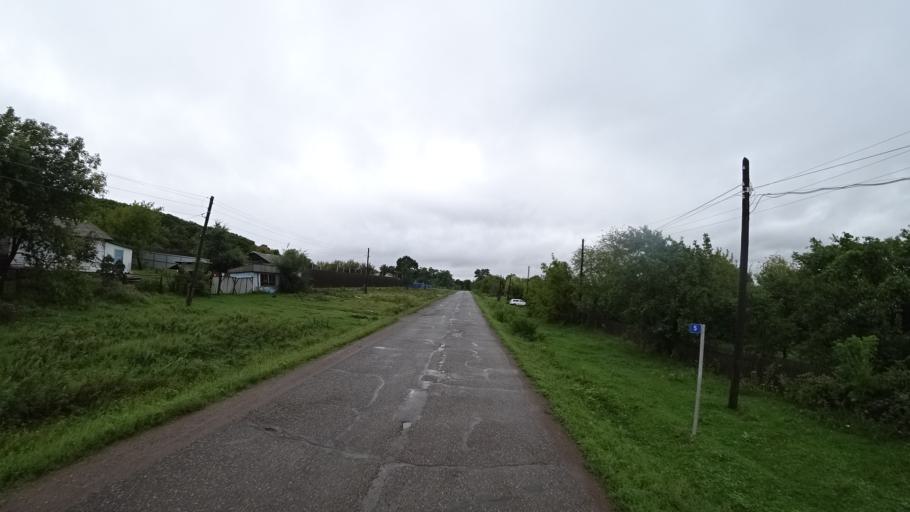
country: RU
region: Primorskiy
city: Monastyrishche
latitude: 44.2647
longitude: 132.4206
